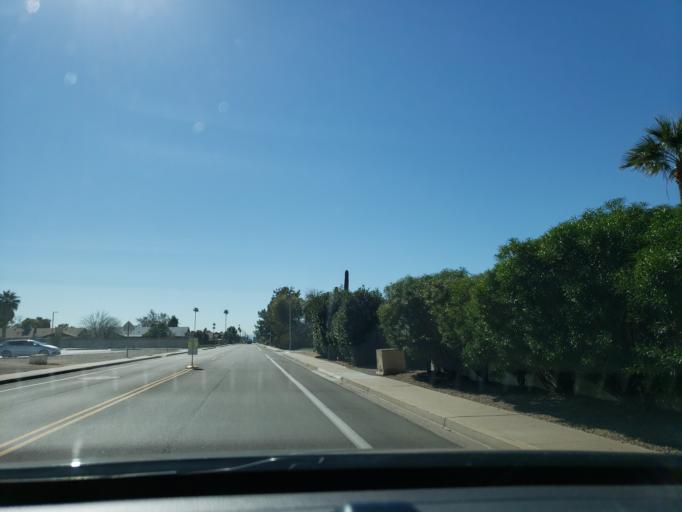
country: US
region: Arizona
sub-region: Maricopa County
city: Glendale
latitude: 33.6166
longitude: -112.1252
